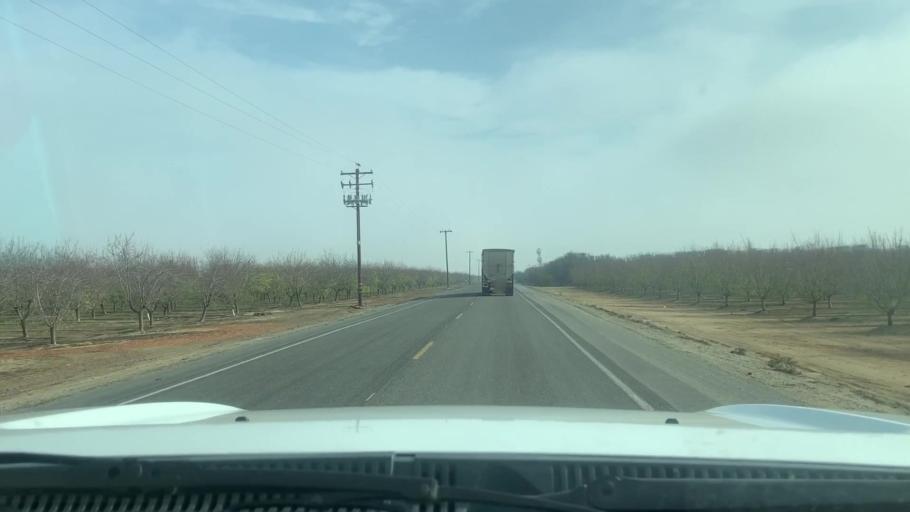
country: US
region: California
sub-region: Kern County
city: Buttonwillow
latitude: 35.5004
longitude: -119.4184
